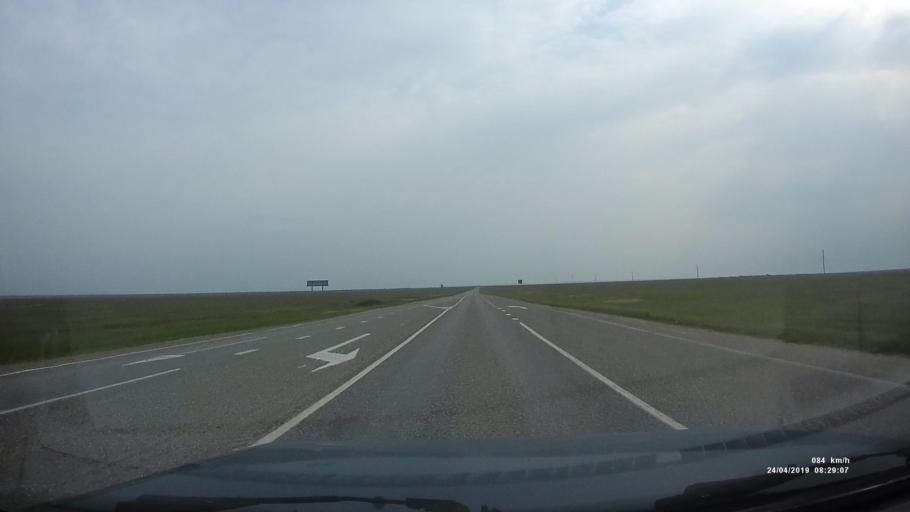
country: RU
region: Kalmykiya
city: Priyutnoye
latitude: 46.1496
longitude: 43.8256
